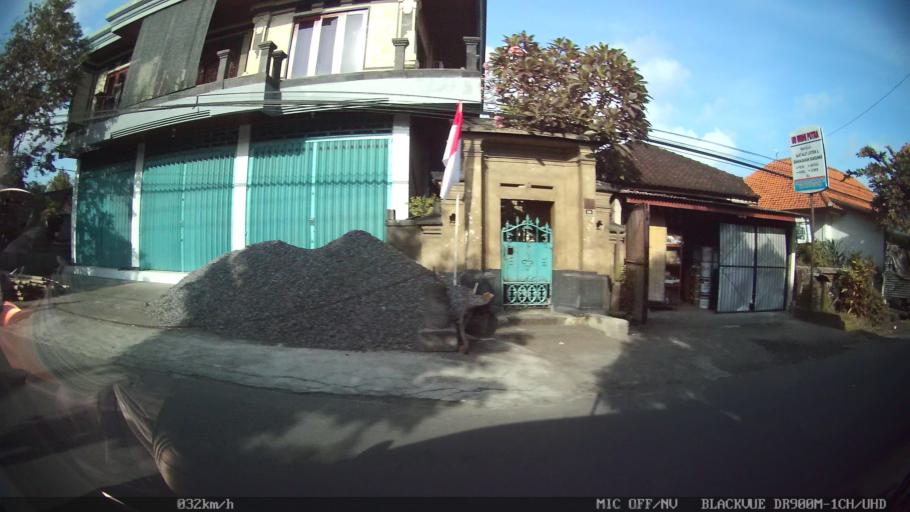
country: ID
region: Bali
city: Banjar Sedang
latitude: -8.5699
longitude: 115.2374
